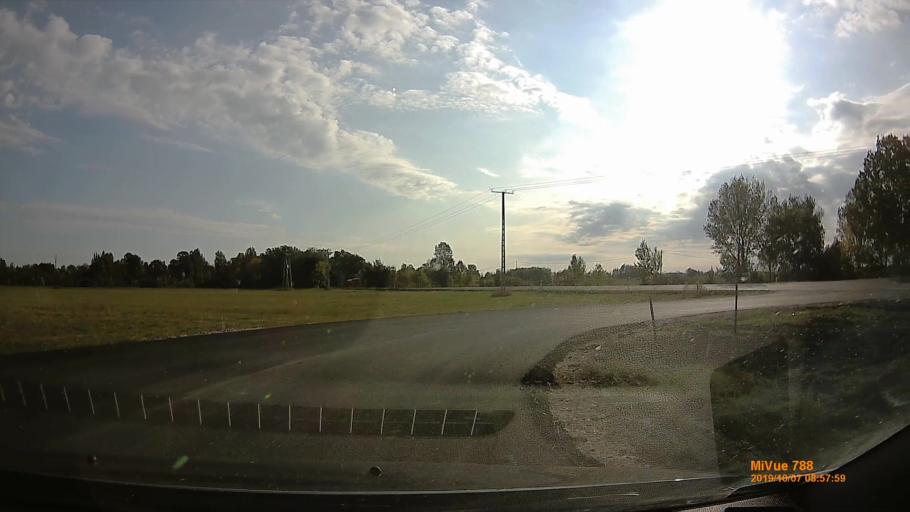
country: HU
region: Bekes
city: Szarvas
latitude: 46.8207
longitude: 20.5237
